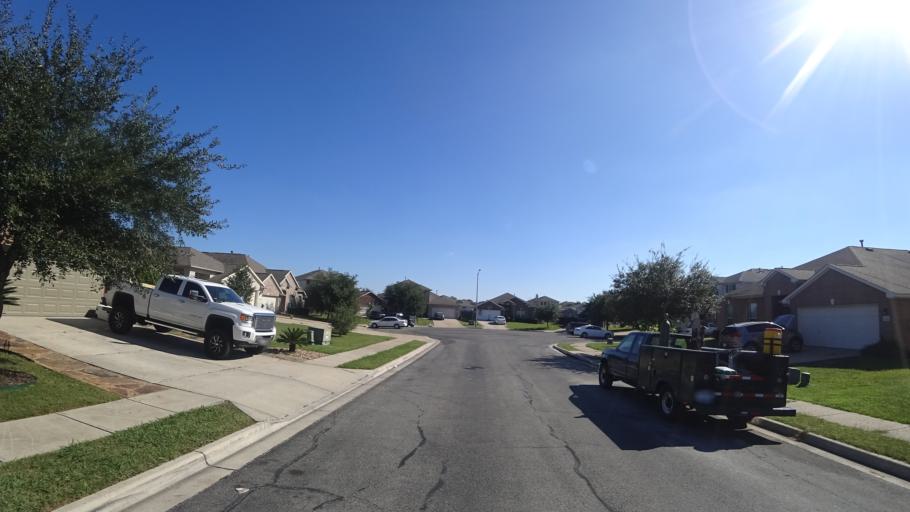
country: US
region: Texas
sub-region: Travis County
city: Manor
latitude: 30.3559
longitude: -97.6113
